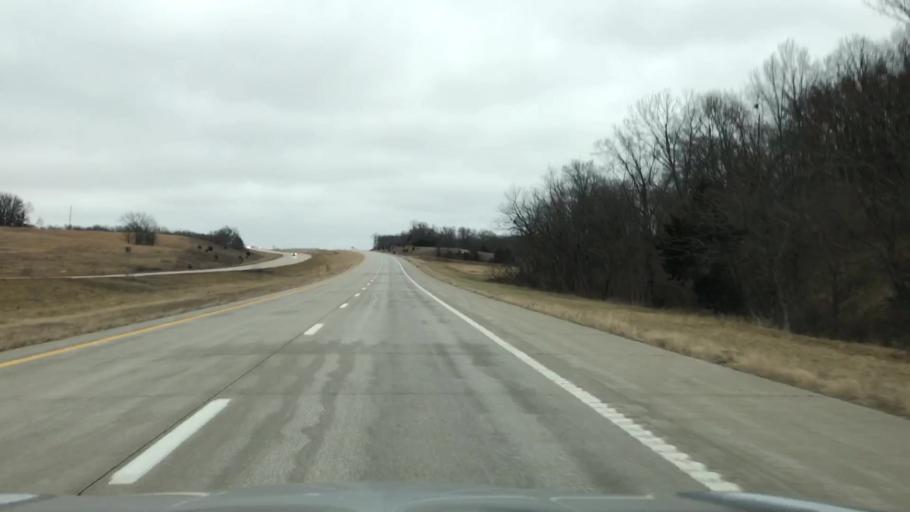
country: US
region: Missouri
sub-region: Linn County
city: Marceline
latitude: 39.7604
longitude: -92.8024
